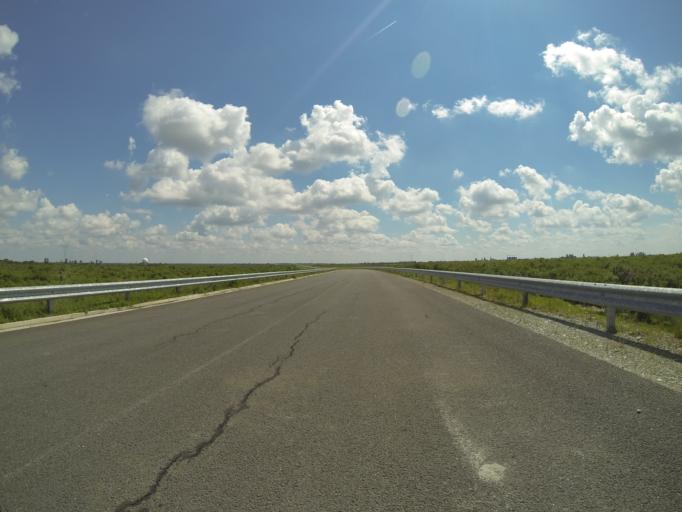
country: RO
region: Dolj
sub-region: Comuna Carcea
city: Carcea
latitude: 44.2845
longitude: 23.9061
